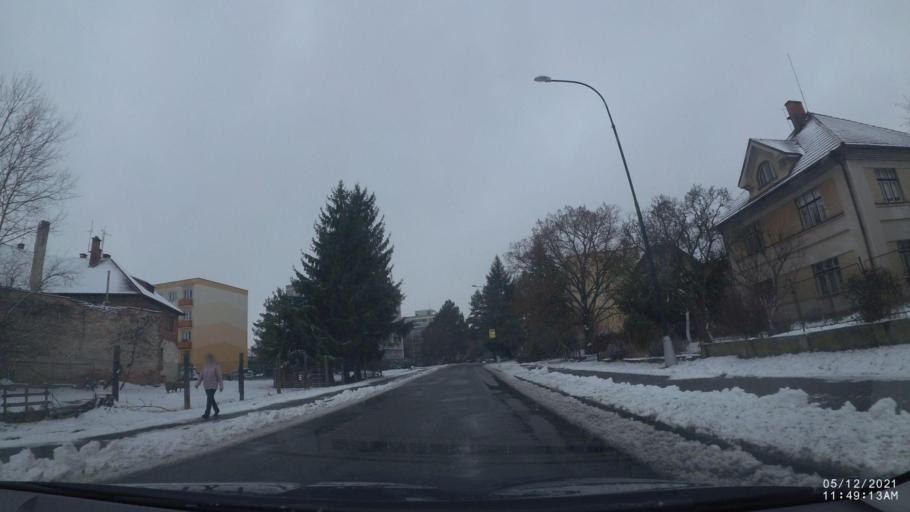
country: CZ
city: Dobruska
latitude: 50.2896
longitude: 16.1646
